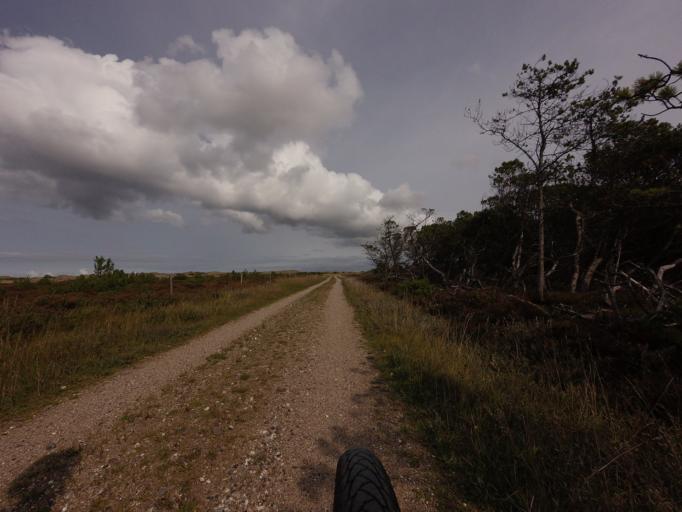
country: DK
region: North Denmark
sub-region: Frederikshavn Kommune
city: Strandby
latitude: 57.6387
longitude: 10.4002
